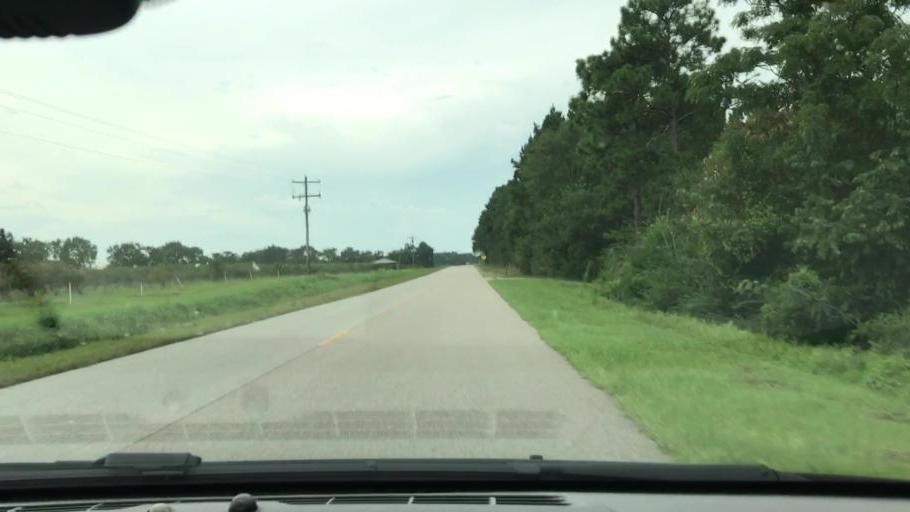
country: US
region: Alabama
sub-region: Houston County
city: Ashford
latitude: 31.2601
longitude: -85.1667
